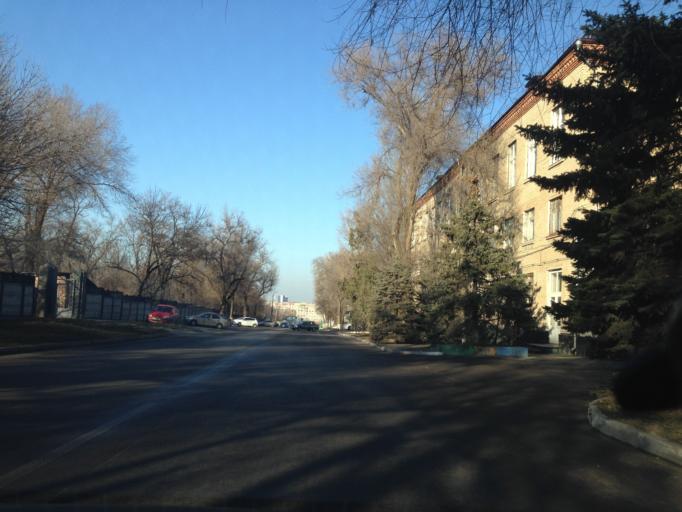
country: RU
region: Rostov
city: Rostov-na-Donu
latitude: 47.2391
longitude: 39.7189
